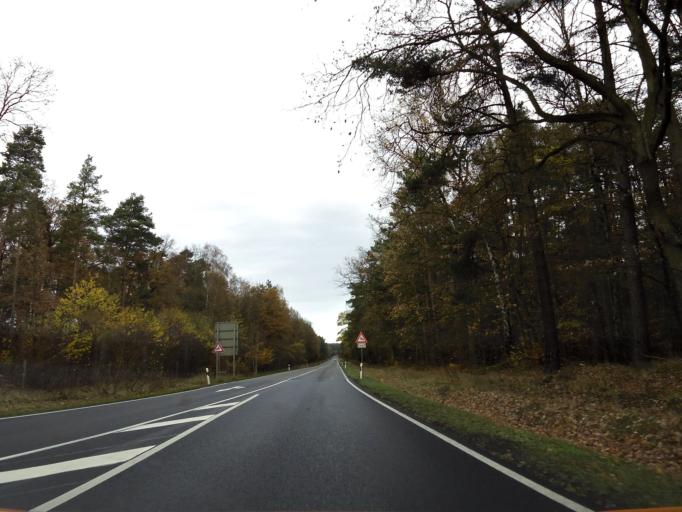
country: DE
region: Saxony-Anhalt
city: Haldensleben I
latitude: 52.3458
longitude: 11.4519
